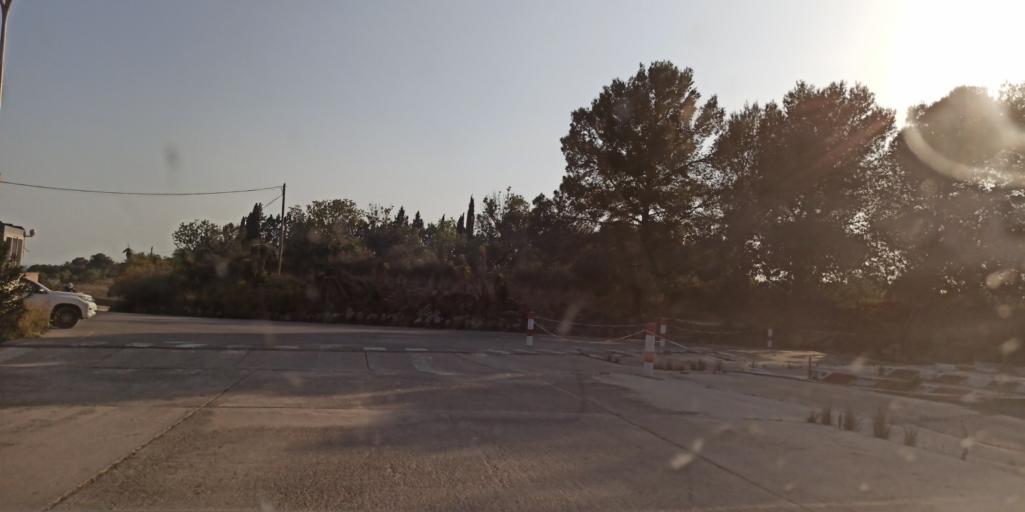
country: ES
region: Catalonia
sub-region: Provincia de Barcelona
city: Sant Feliu de Llobregat
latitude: 41.3990
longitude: 2.0544
